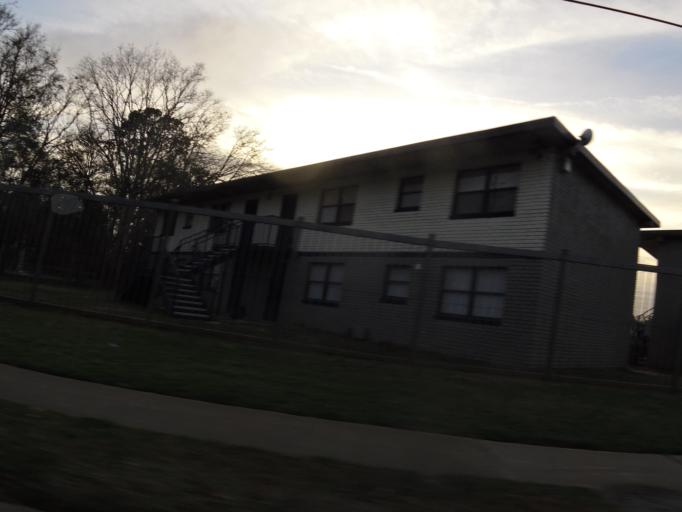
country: US
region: Florida
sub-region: Duval County
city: Jacksonville
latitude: 30.3641
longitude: -81.7060
